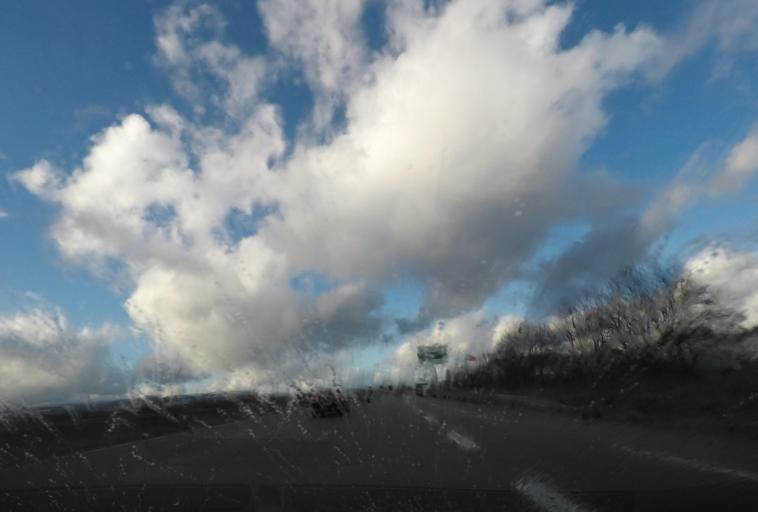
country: FR
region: Ile-de-France
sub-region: Departement de l'Essonne
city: Le Coudray-Montceaux
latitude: 48.5640
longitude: 2.4776
